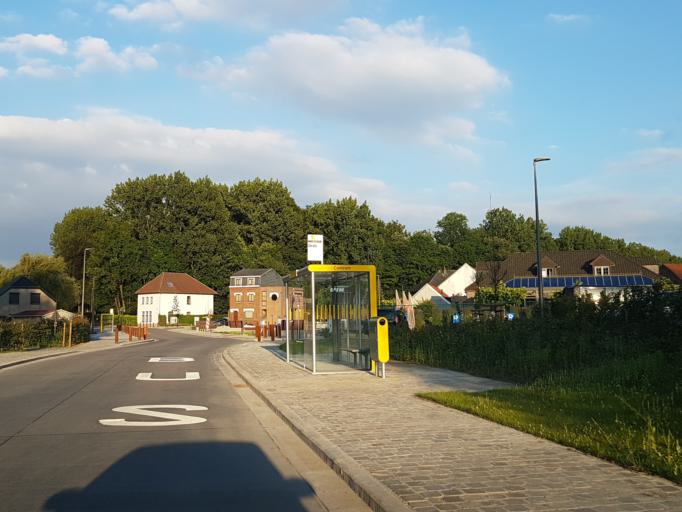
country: BE
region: Flanders
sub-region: Provincie Vlaams-Brabant
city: Ternat
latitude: 50.8617
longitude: 4.2116
